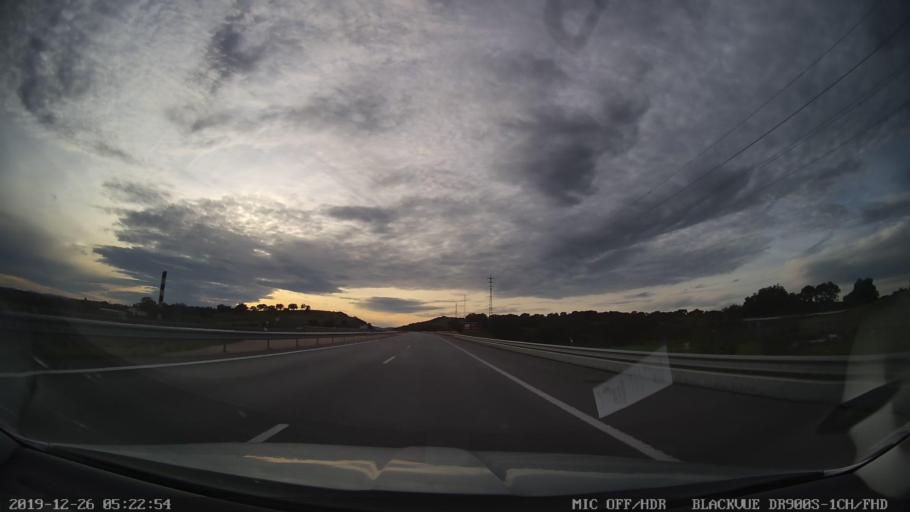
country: PT
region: Evora
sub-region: Vila Vicosa
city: Vila Vicosa
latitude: 38.8488
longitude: -7.3728
